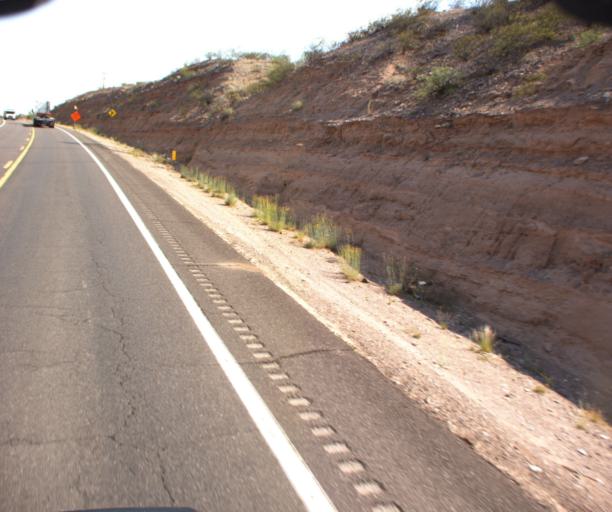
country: US
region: Arizona
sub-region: Greenlee County
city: Clifton
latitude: 32.8892
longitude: -109.1981
